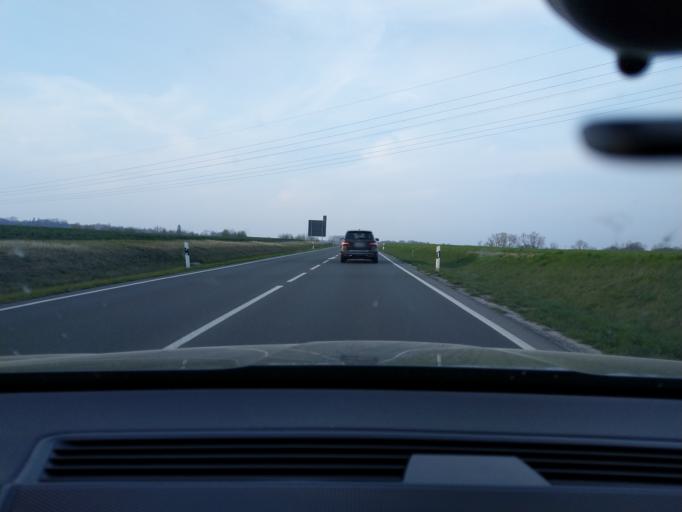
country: DE
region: Mecklenburg-Vorpommern
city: Stralsund
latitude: 54.2889
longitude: 13.0503
